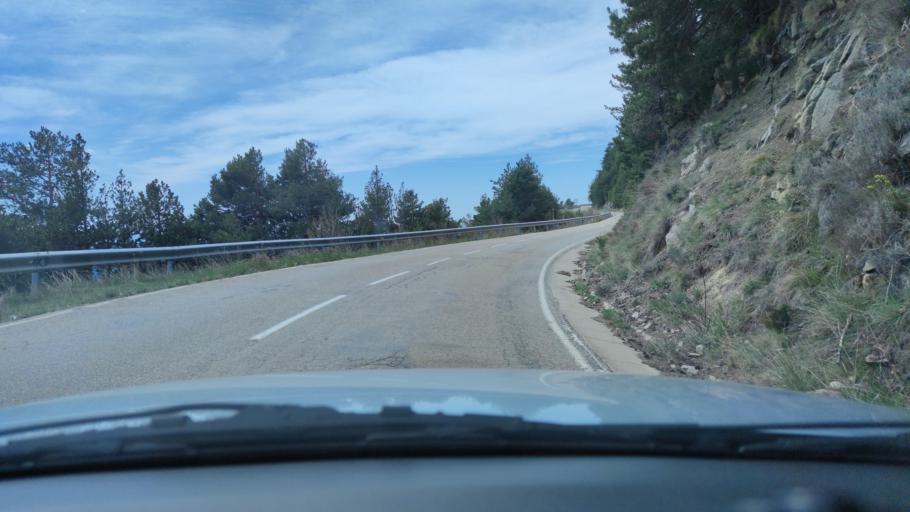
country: ES
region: Catalonia
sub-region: Provincia de Lleida
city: Gosol
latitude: 42.1565
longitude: 1.5735
